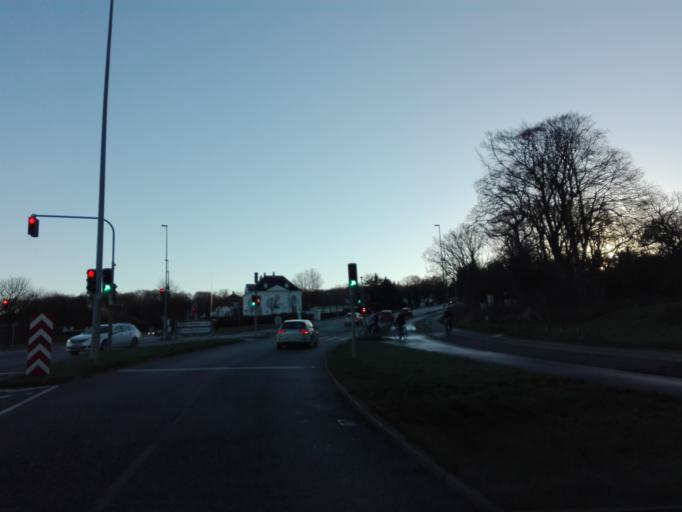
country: DK
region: Central Jutland
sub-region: Arhus Kommune
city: Arhus
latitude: 56.1303
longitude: 10.2130
